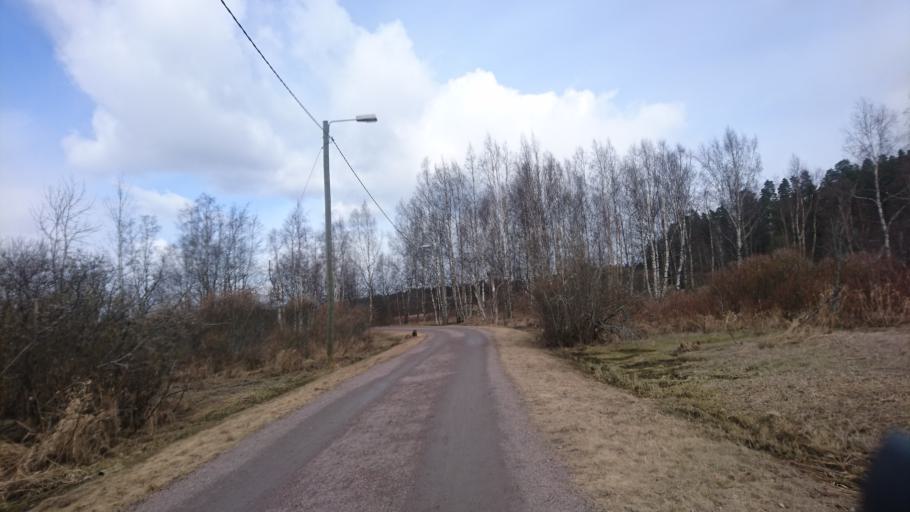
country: FI
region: Uusimaa
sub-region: Helsinki
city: Espoo
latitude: 60.2155
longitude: 24.6774
